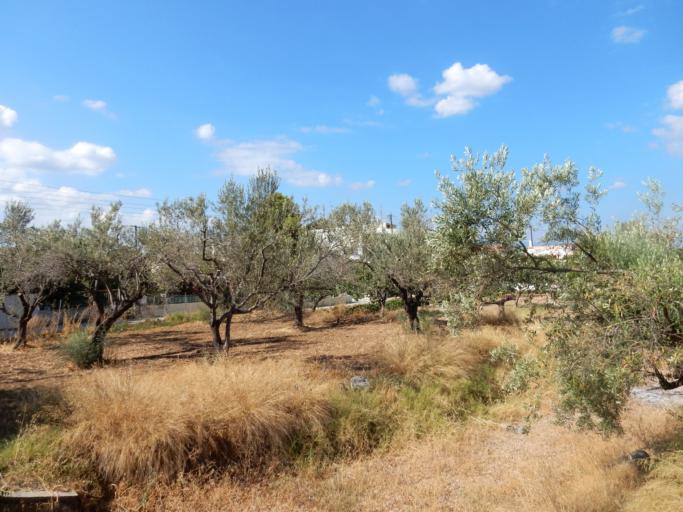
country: GR
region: Attica
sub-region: Nomos Piraios
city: Kypseli
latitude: 37.7189
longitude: 23.4611
